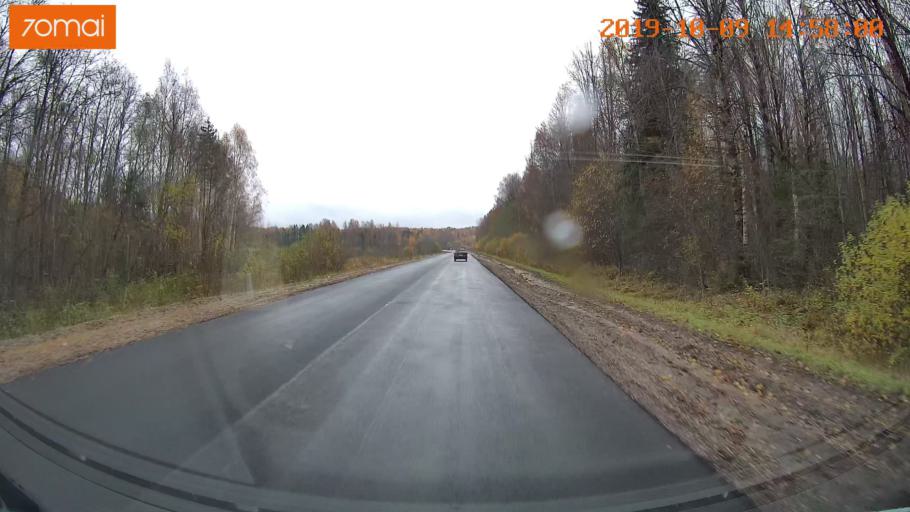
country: RU
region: Kostroma
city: Chistyye Bory
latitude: 58.3315
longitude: 41.6532
